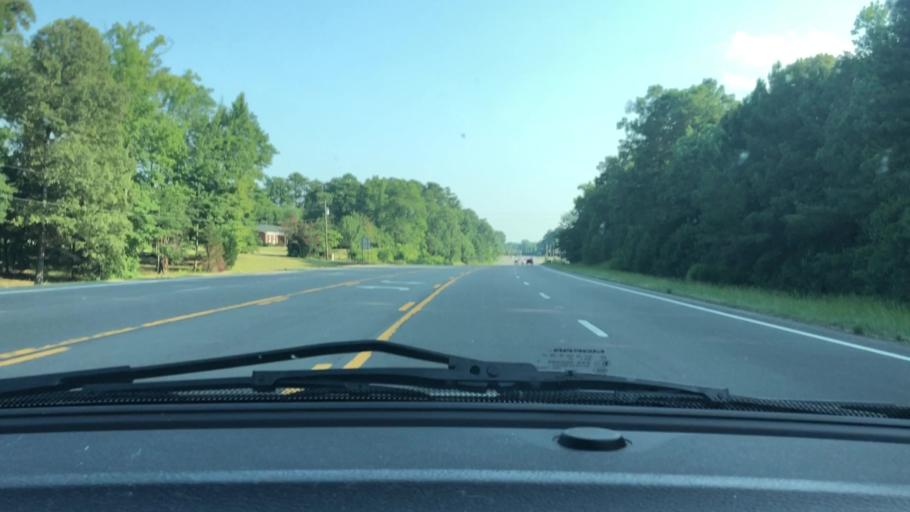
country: US
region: North Carolina
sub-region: Lee County
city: Broadway
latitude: 35.3861
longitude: -79.1078
